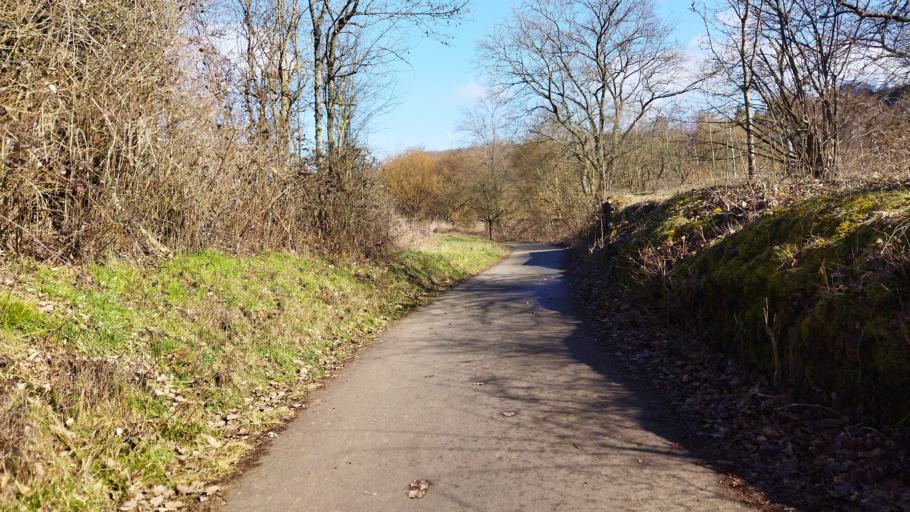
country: DE
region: Rheinland-Pfalz
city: Altenglan
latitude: 49.5359
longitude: 7.4592
